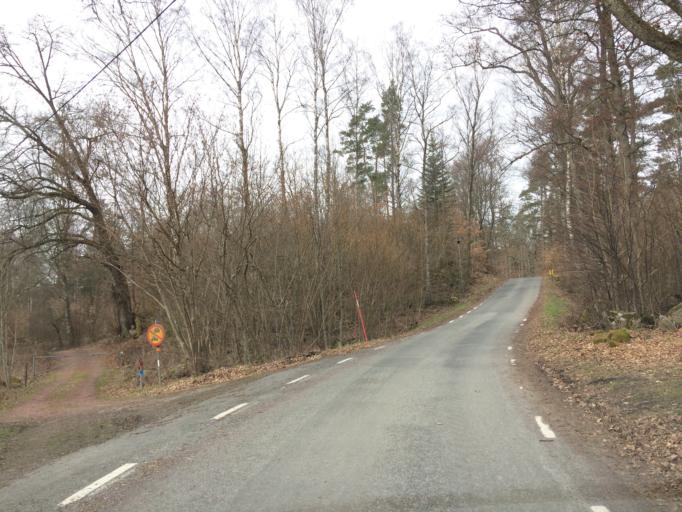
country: SE
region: Skane
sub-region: Ostra Goinge Kommun
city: Sibbhult
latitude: 56.2804
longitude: 14.3032
